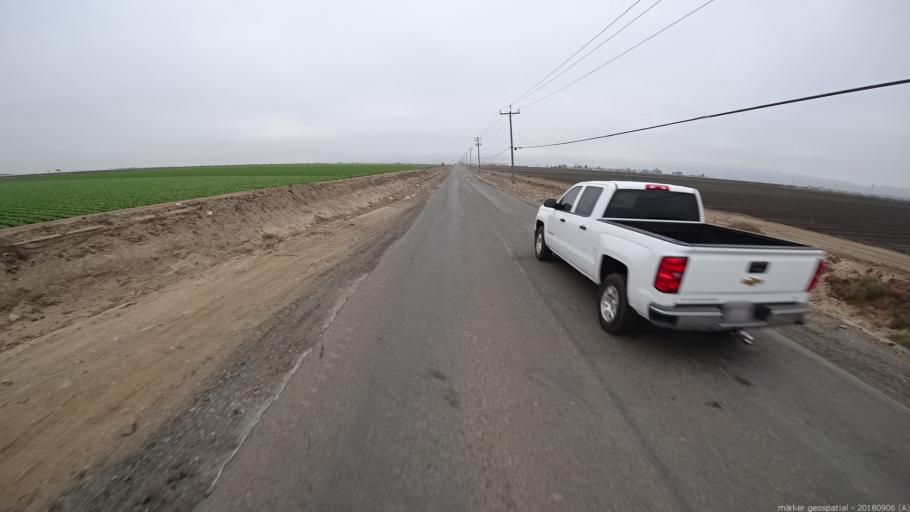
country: US
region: California
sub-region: Monterey County
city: Salinas
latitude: 36.6406
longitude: -121.5790
